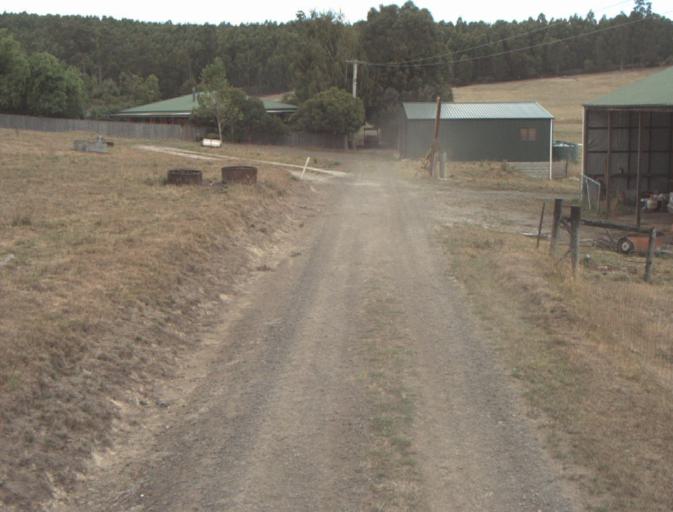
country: AU
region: Tasmania
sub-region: Launceston
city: Mayfield
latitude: -41.2406
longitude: 147.1858
